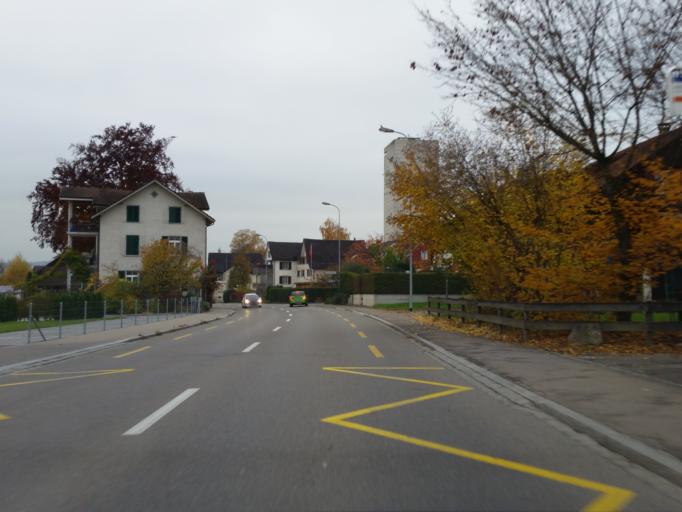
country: CH
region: Thurgau
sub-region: Arbon District
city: Amriswil
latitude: 47.5559
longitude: 9.3257
